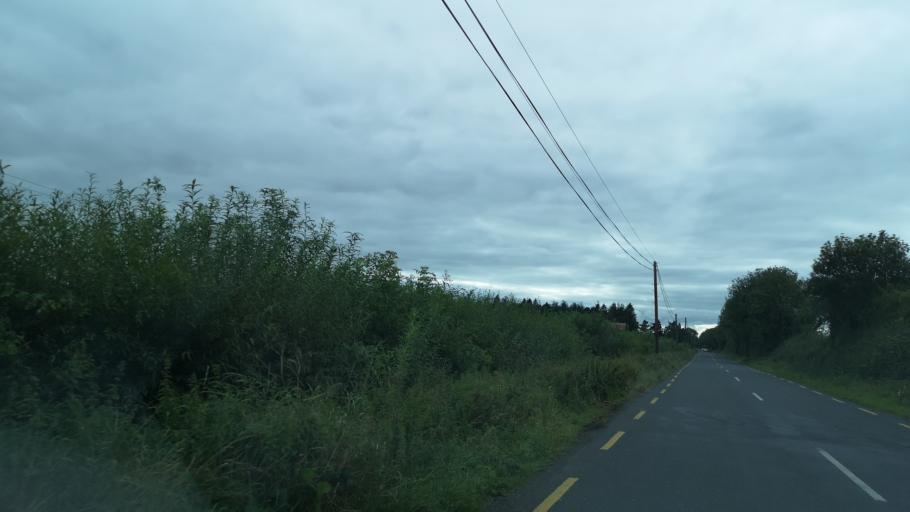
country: IE
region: Leinster
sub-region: Uibh Fhaili
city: Ferbane
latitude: 53.2294
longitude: -7.7842
